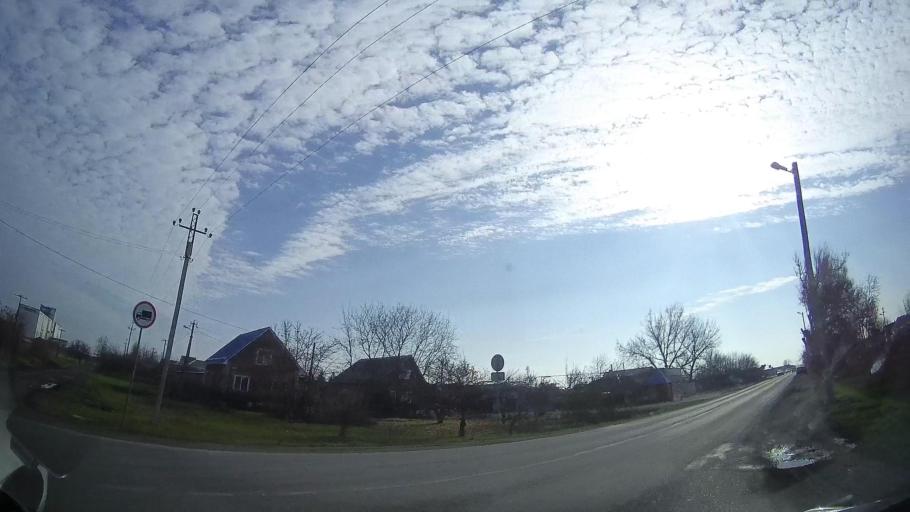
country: RU
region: Rostov
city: Tselina
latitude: 46.5369
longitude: 41.0508
